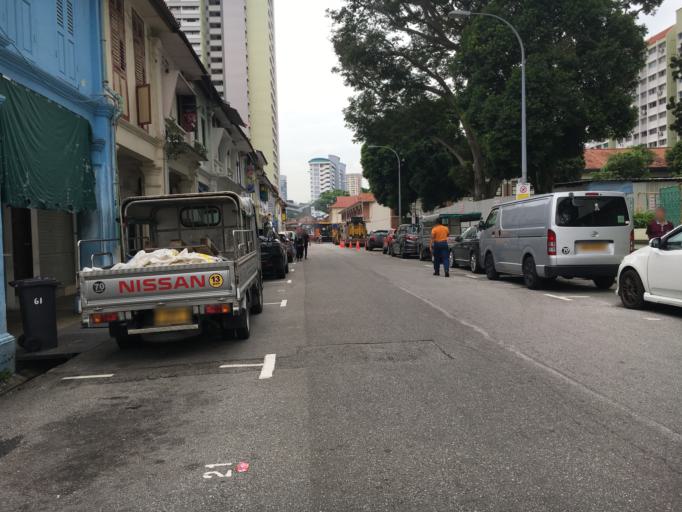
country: SG
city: Singapore
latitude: 1.3084
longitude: 103.8551
